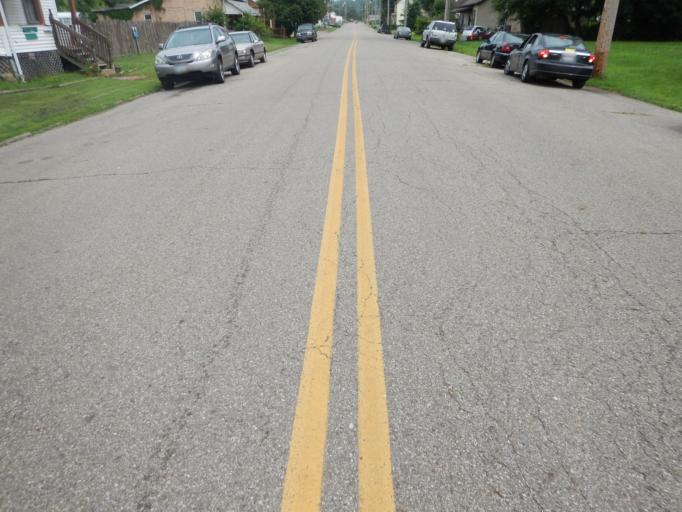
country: US
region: Ohio
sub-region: Muskingum County
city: Zanesville
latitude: 39.9468
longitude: -82.0175
